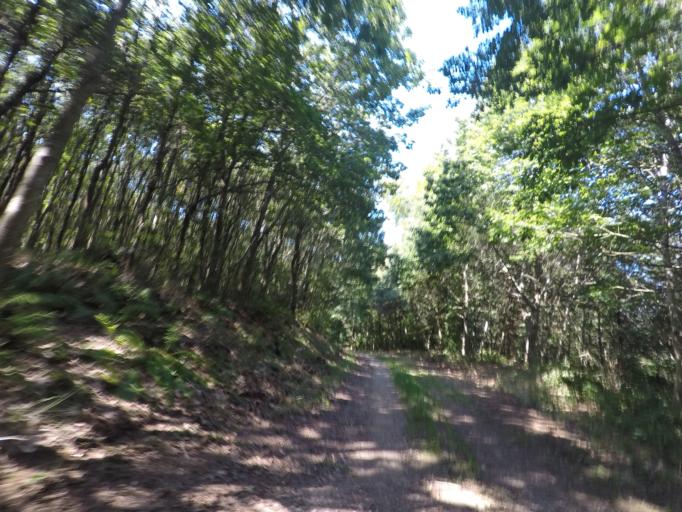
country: LU
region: Luxembourg
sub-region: Canton de Capellen
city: Kopstal
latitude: 49.6560
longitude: 6.0719
